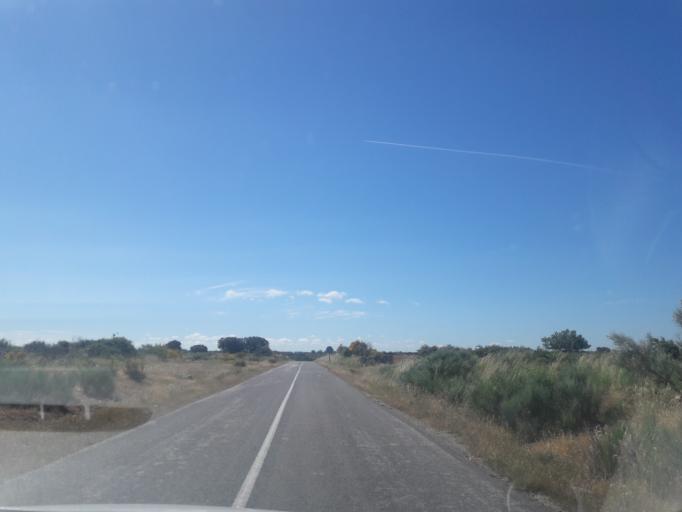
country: ES
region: Castille and Leon
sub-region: Provincia de Salamanca
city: Lumbrales
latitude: 40.9651
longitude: -6.7260
